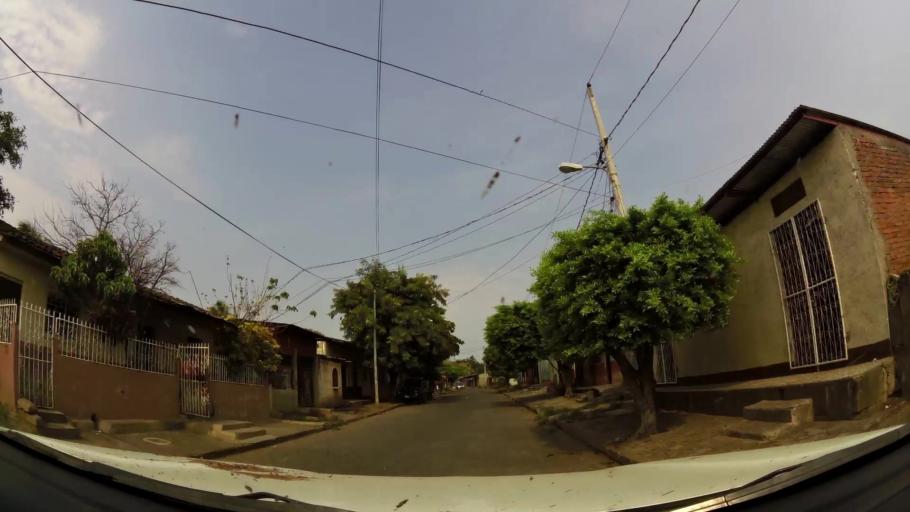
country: NI
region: Masaya
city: Masaya
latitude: 11.9717
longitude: -86.0904
